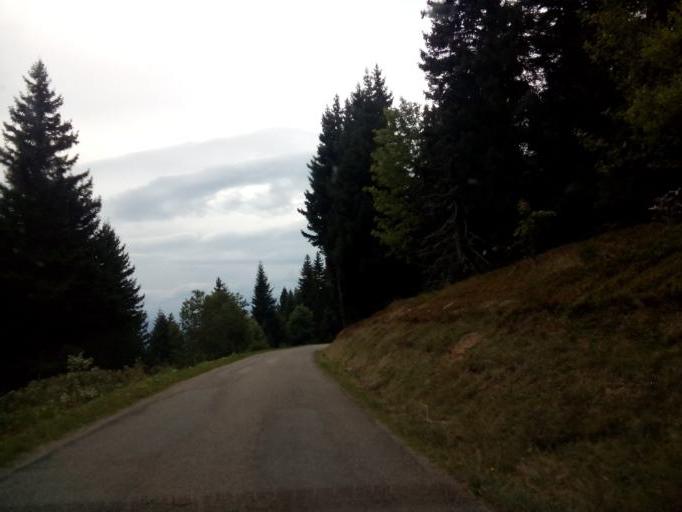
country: FR
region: Rhone-Alpes
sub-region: Departement de l'Isere
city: Vaulnaveys-le-Bas
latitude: 45.0337
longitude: 5.8599
